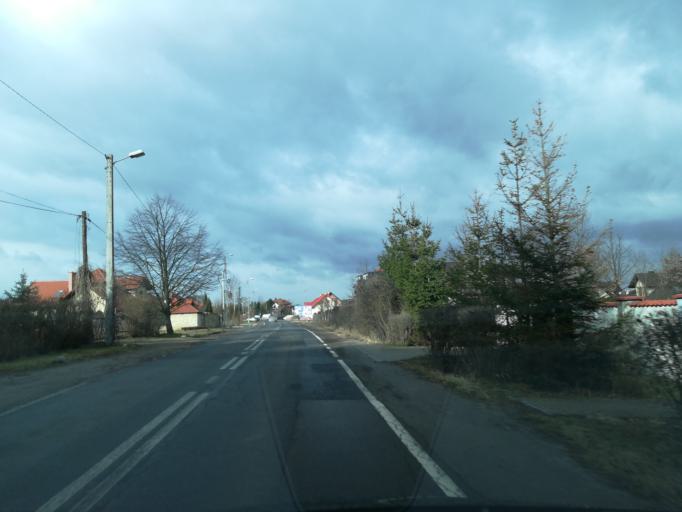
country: PL
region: Lesser Poland Voivodeship
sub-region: Powiat krakowski
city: Libertow
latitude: 49.9832
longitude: 19.8883
